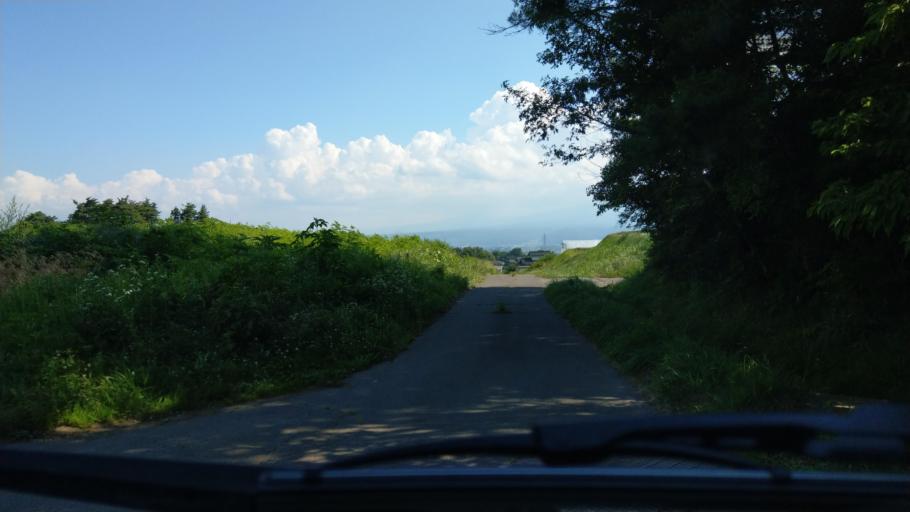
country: JP
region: Nagano
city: Komoro
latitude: 36.3260
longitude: 138.4502
